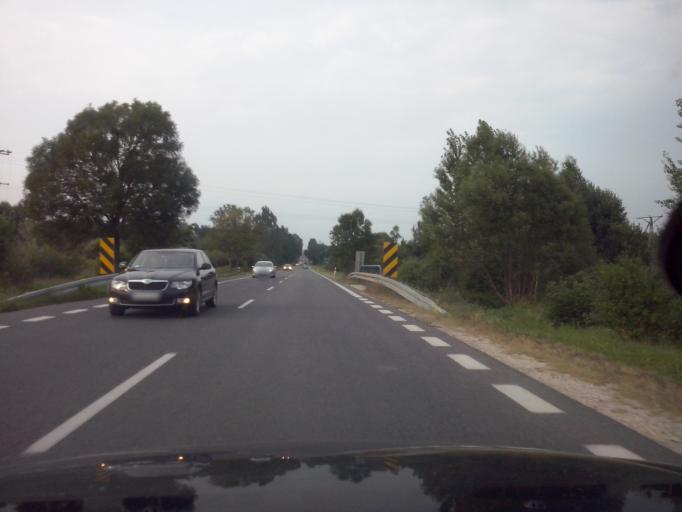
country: PL
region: Swietokrzyskie
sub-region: Powiat kielecki
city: Morawica
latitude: 50.7598
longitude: 20.6186
